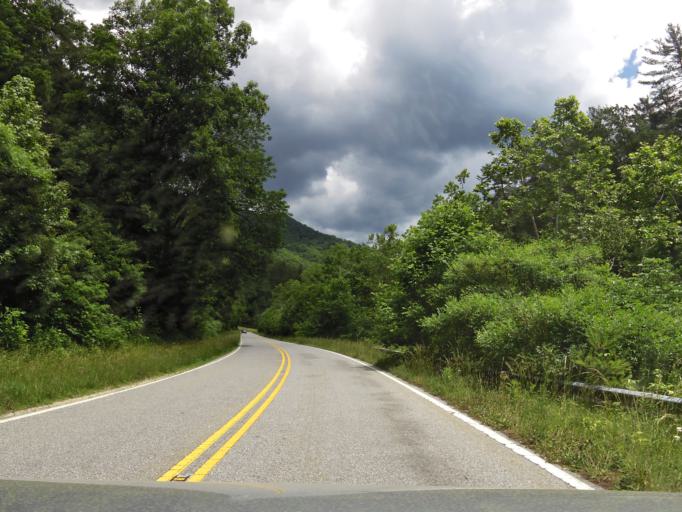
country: US
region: North Carolina
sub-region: Graham County
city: Robbinsville
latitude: 35.3977
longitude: -83.8716
